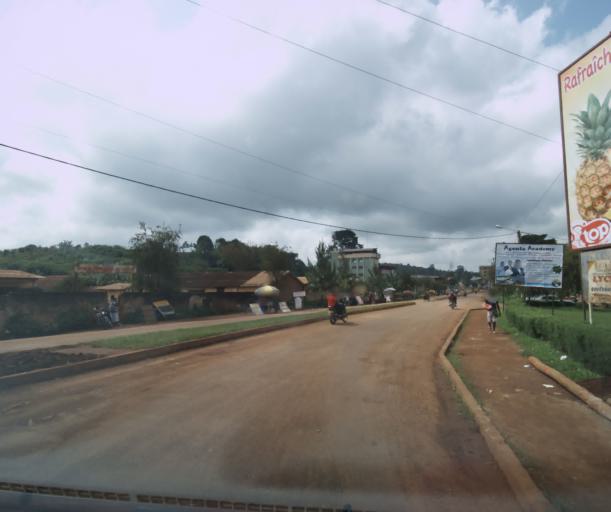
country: CM
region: West
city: Dschang
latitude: 5.4490
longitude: 10.0615
